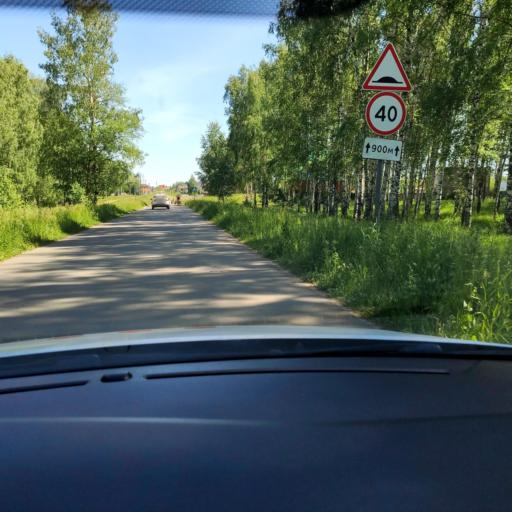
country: RU
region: Tatarstan
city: Staroye Arakchino
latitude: 55.8882
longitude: 49.0351
